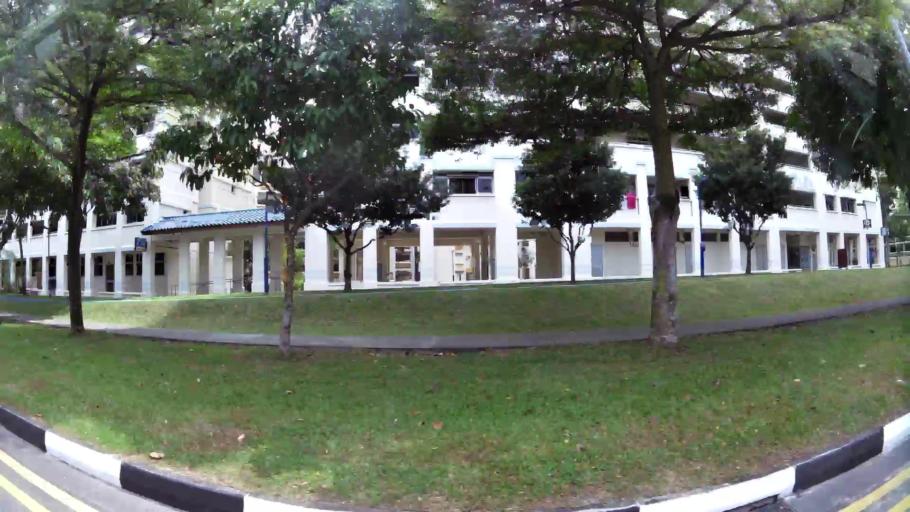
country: MY
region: Johor
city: Johor Bahru
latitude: 1.3504
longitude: 103.6998
